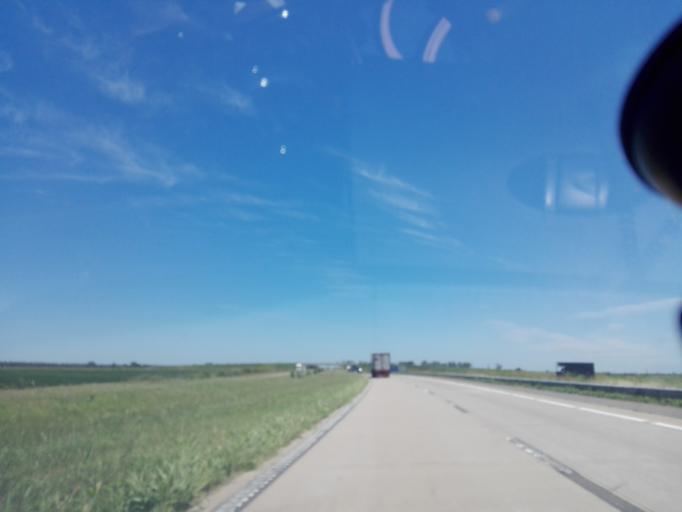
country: AR
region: Cordoba
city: General Roca
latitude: -32.6948
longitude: -61.9573
